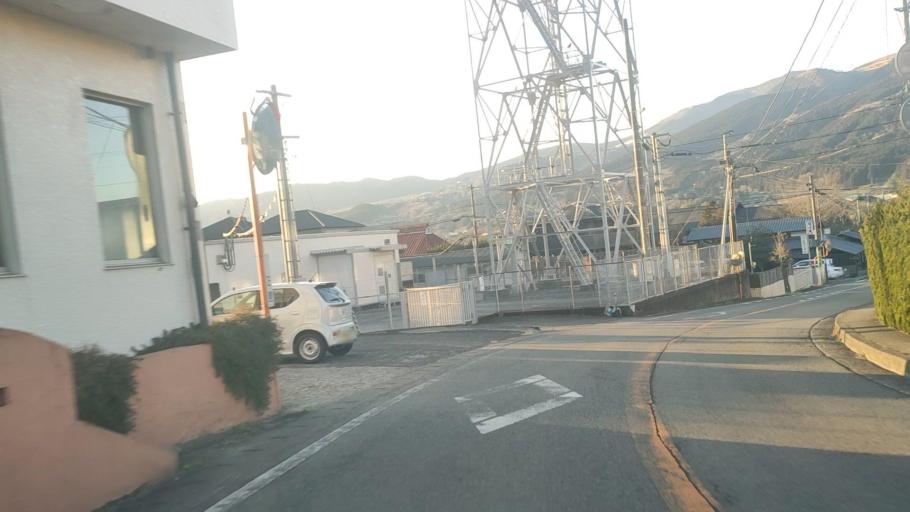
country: JP
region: Oita
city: Beppu
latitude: 33.2568
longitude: 131.3581
